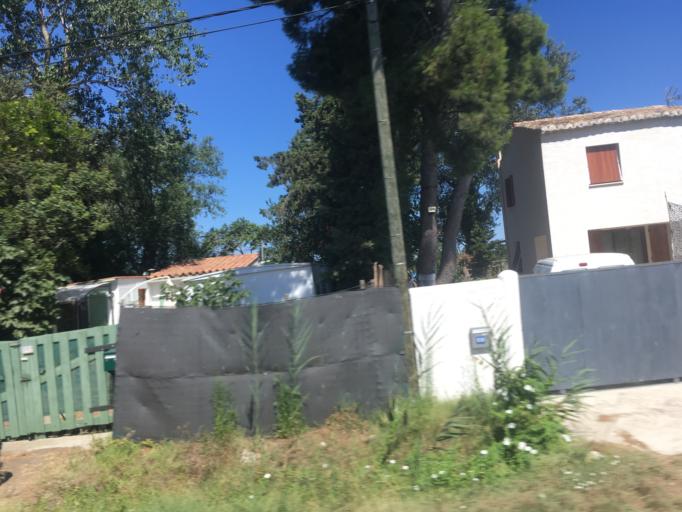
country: FR
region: Languedoc-Roussillon
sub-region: Departement du Gard
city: Saint-Gilles
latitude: 43.5843
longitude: 4.4675
